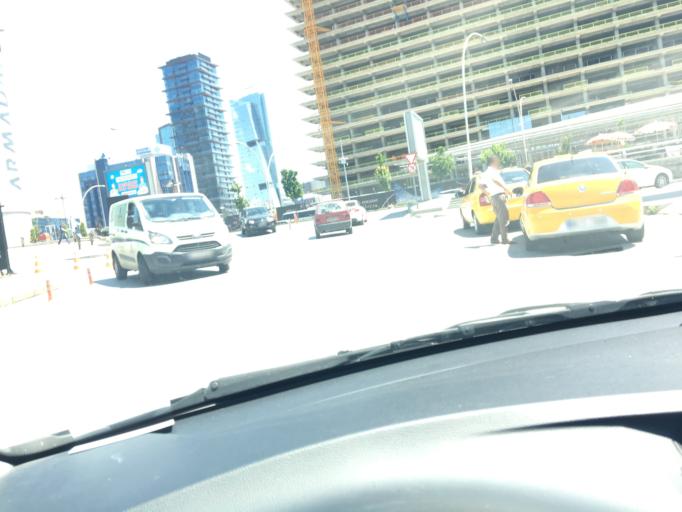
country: TR
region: Ankara
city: Ankara
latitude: 39.9120
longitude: 32.8086
